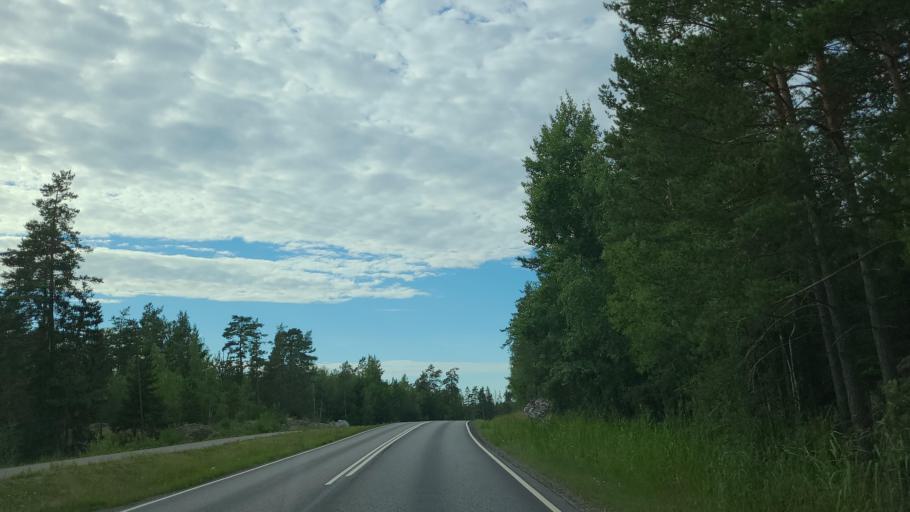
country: FI
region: Varsinais-Suomi
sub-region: Turku
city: Rymaettylae
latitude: 60.3954
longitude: 21.9010
